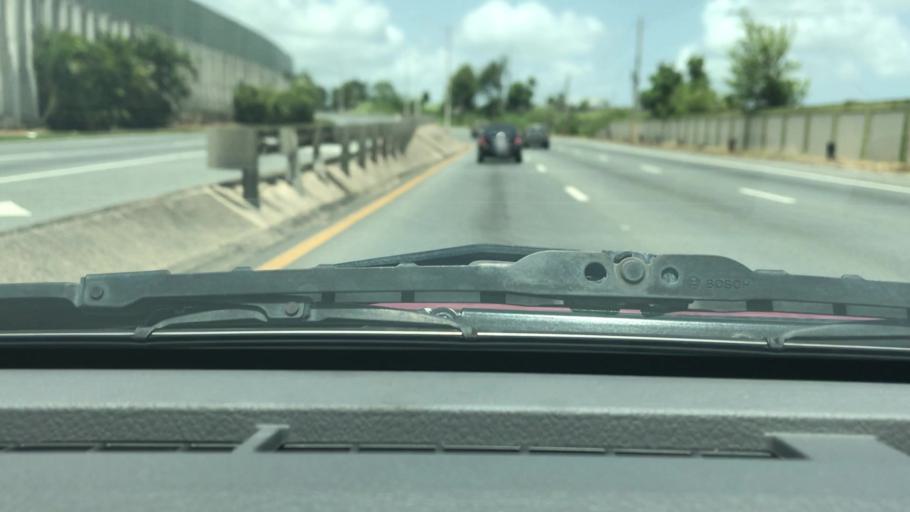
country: PR
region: Toa Alta
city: Pajaros
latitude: 18.3646
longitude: -66.1842
